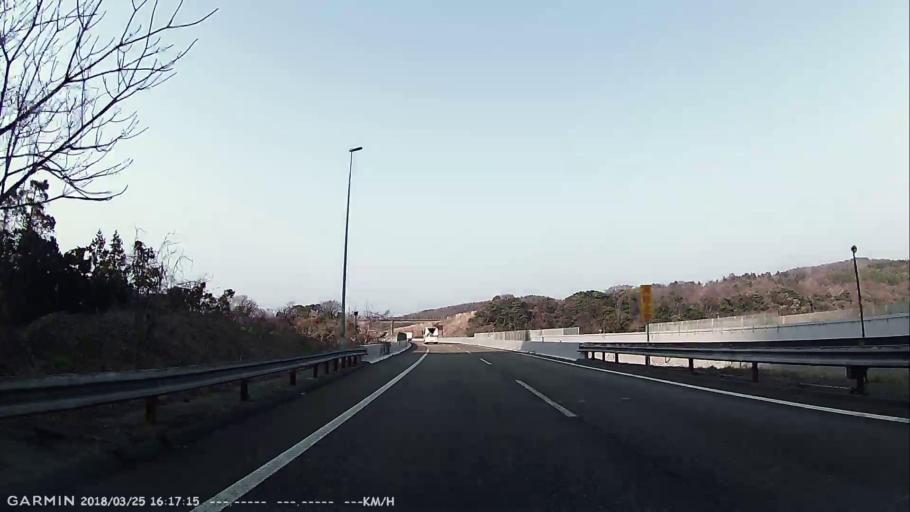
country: JP
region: Niigata
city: Kashiwazaki
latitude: 37.3179
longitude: 138.4523
